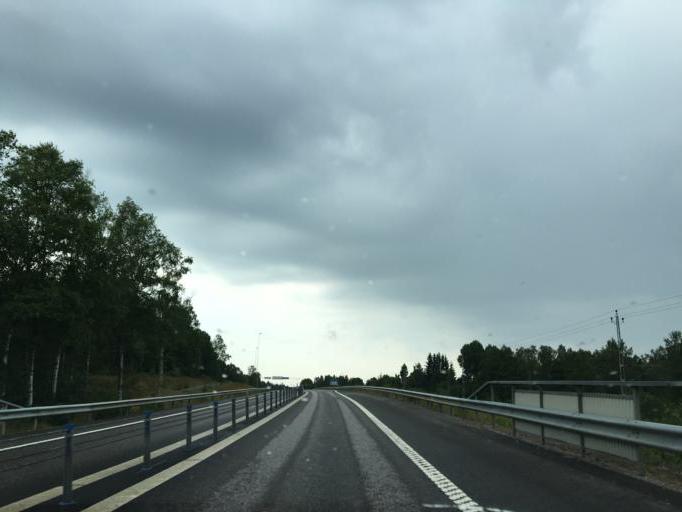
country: SE
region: OEstergoetland
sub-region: Norrkopings Kommun
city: Jursla
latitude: 58.7844
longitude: 16.1573
